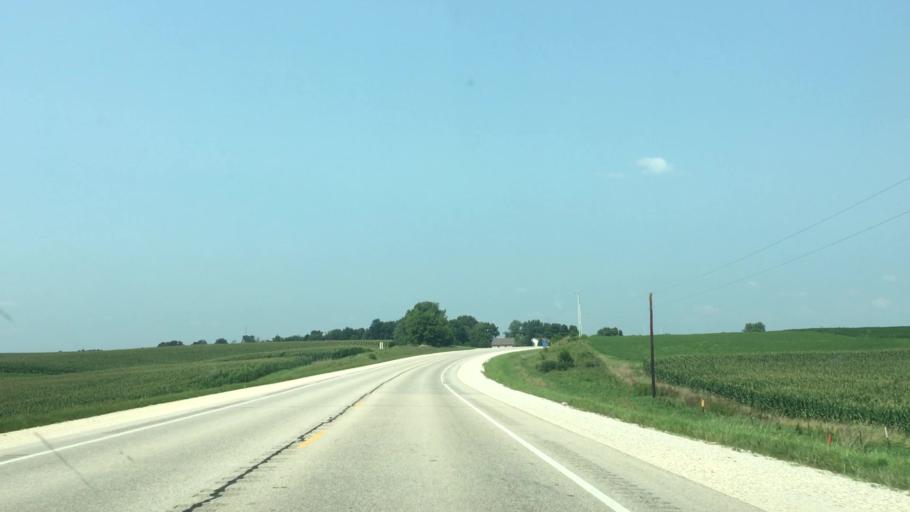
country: US
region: Iowa
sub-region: Winneshiek County
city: Decorah
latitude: 43.2590
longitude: -91.8381
